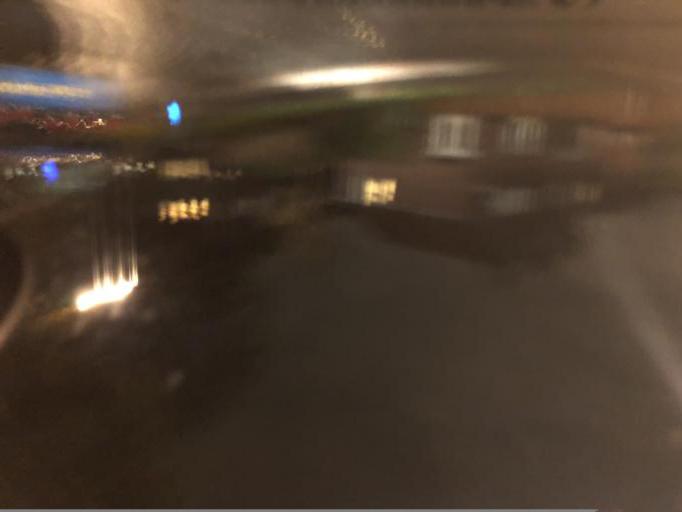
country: GB
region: England
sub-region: Borough of Oldham
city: Shaw
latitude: 53.5493
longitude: -2.0824
